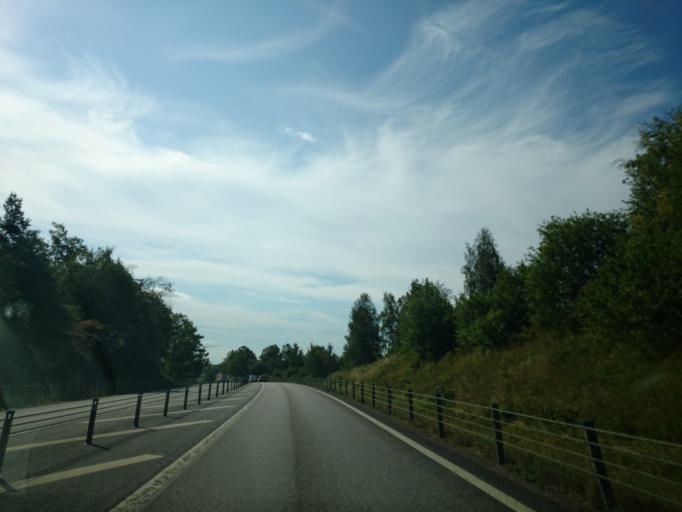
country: SE
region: Kalmar
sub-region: Vasterviks Kommun
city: Gamleby
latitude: 57.8840
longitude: 16.3888
